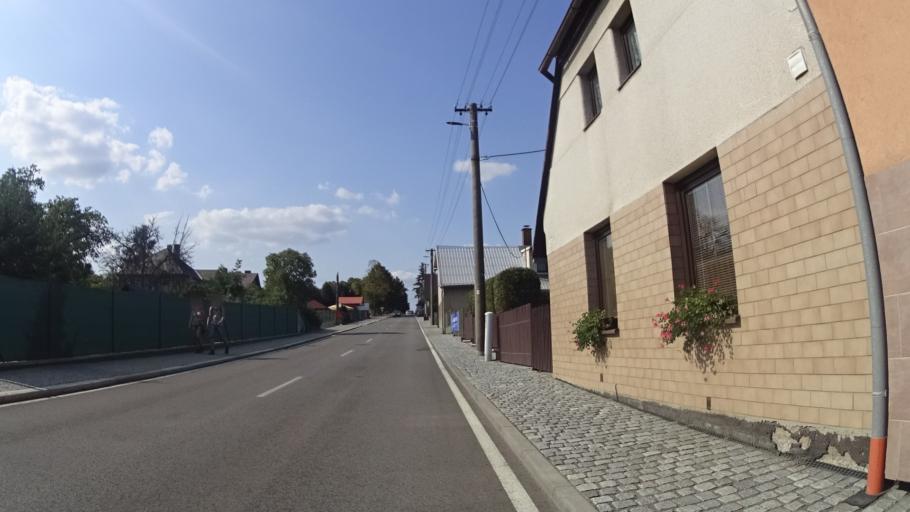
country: CZ
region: Kralovehradecky
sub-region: Okres Jicin
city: Sobotka
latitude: 50.4696
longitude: 15.1759
